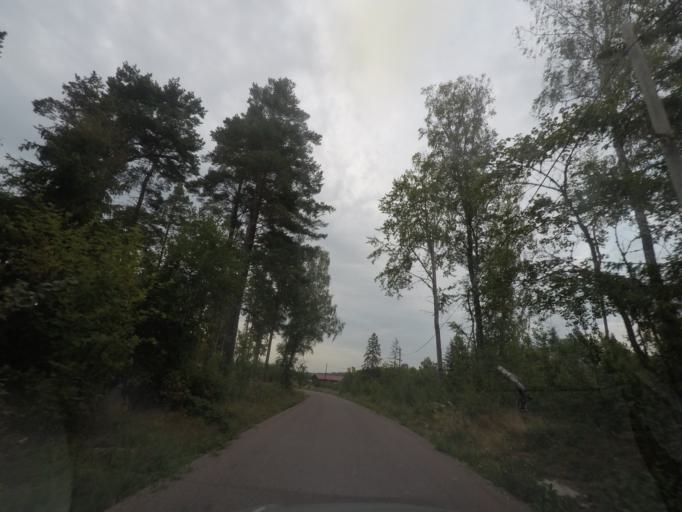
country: SE
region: Vaestmanland
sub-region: Hallstahammars Kommun
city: Kolback
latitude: 59.5036
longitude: 16.1915
